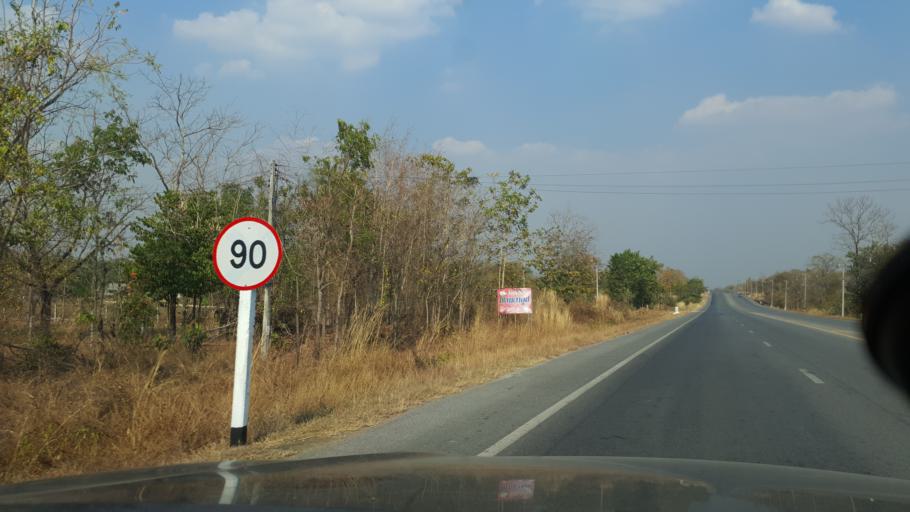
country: TH
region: Sukhothai
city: Ban Dan Lan Hoi
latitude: 16.9515
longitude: 99.4420
